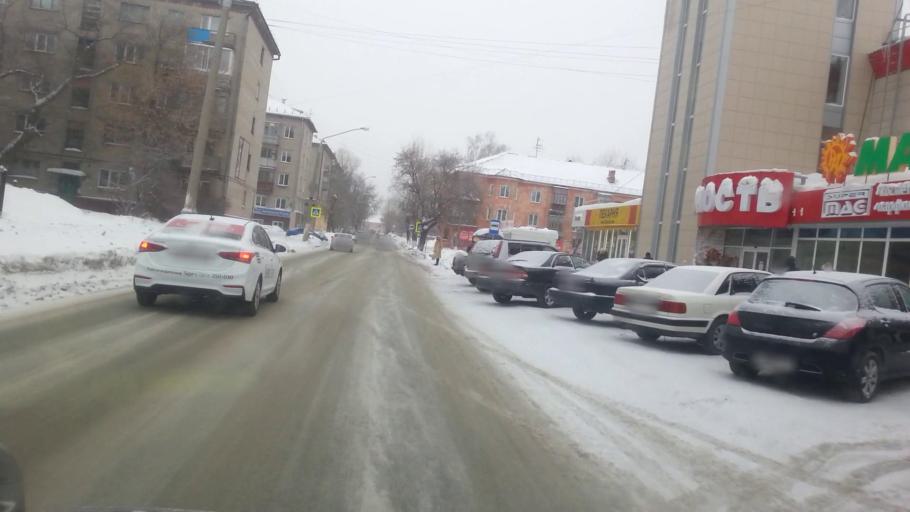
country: RU
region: Altai Krai
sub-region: Gorod Barnaulskiy
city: Barnaul
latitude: 53.3793
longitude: 83.7234
